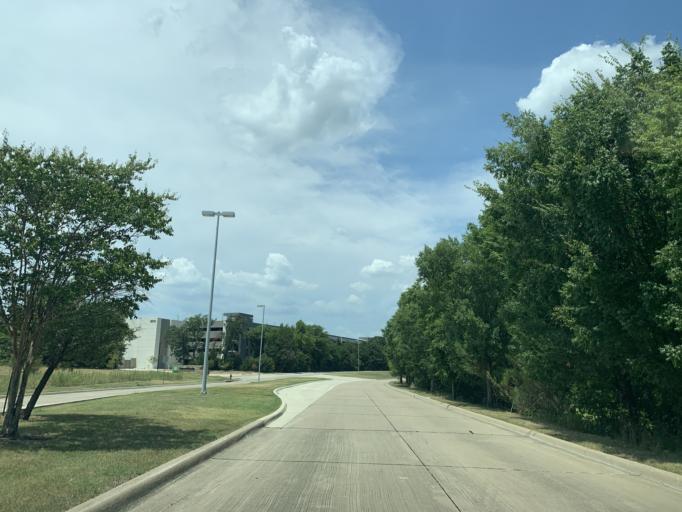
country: US
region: Texas
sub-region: Denton County
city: Trophy Club
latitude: 32.9769
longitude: -97.1576
